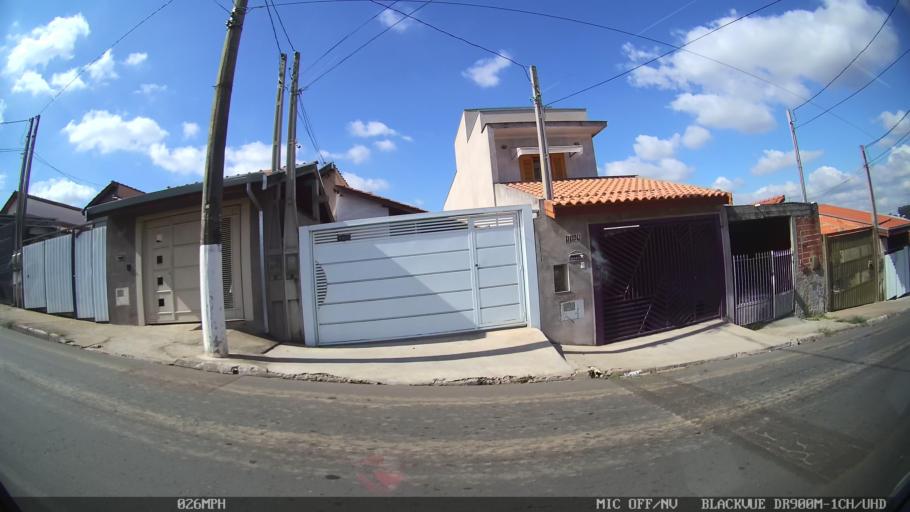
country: BR
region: Sao Paulo
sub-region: Hortolandia
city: Hortolandia
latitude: -22.8860
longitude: -47.2034
